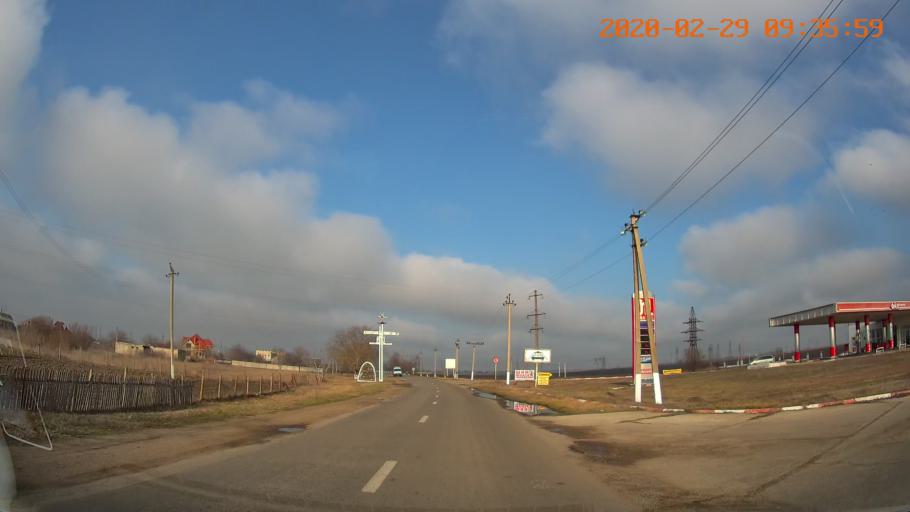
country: MD
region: Telenesti
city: Dnestrovsc
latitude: 46.6221
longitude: 29.8937
